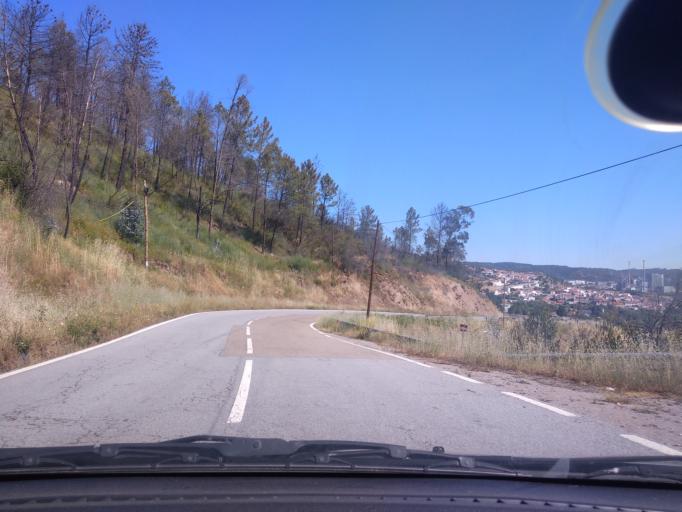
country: PT
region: Portalegre
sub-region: Nisa
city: Nisa
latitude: 39.6434
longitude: -7.6701
